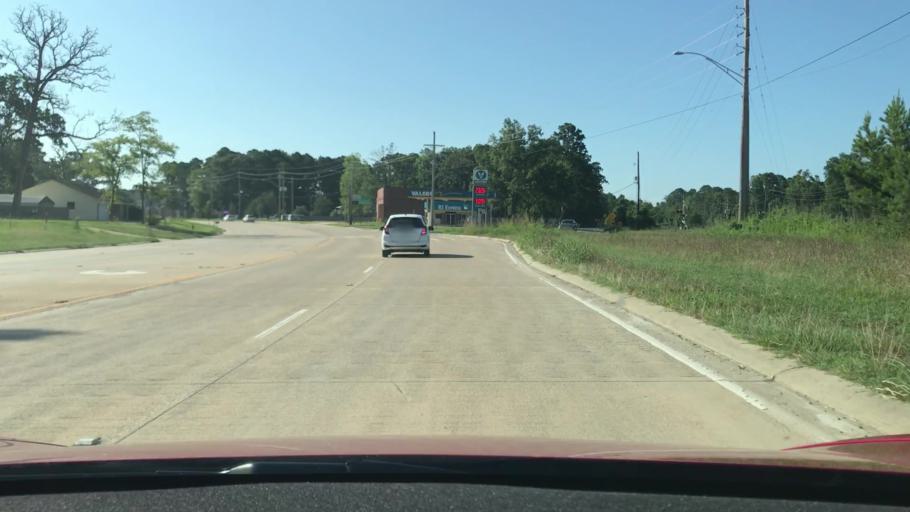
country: US
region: Louisiana
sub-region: Bossier Parish
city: Bossier City
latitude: 32.3999
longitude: -93.7350
